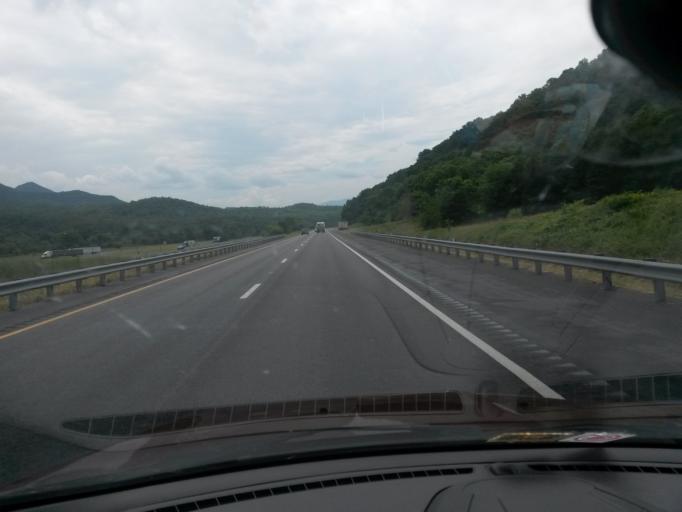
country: US
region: Virginia
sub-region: Alleghany County
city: Clifton Forge
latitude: 37.7992
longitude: -79.7095
